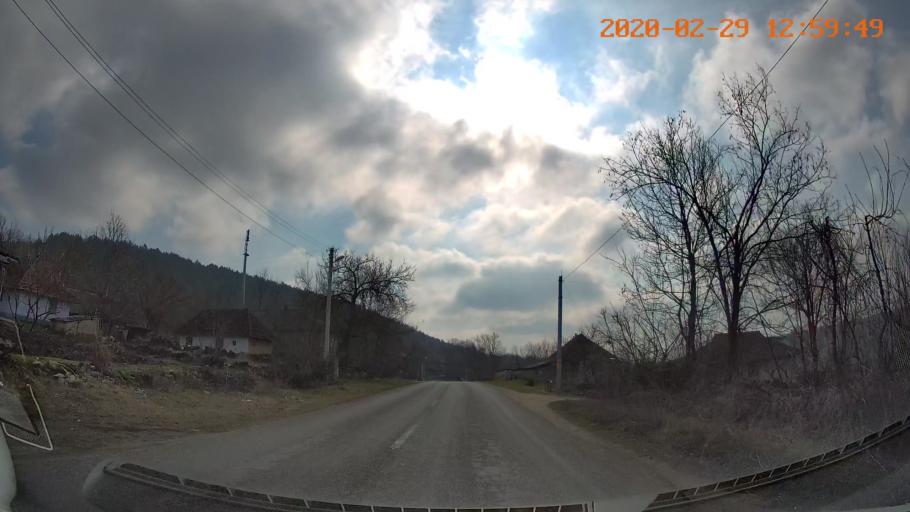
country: MD
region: Telenesti
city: Camenca
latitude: 48.0582
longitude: 28.7249
